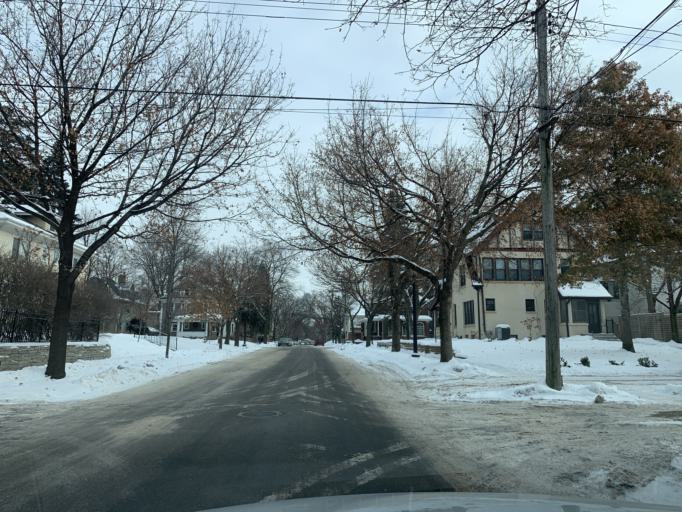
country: US
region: Minnesota
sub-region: Hennepin County
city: Minneapolis
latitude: 44.9610
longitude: -93.2990
